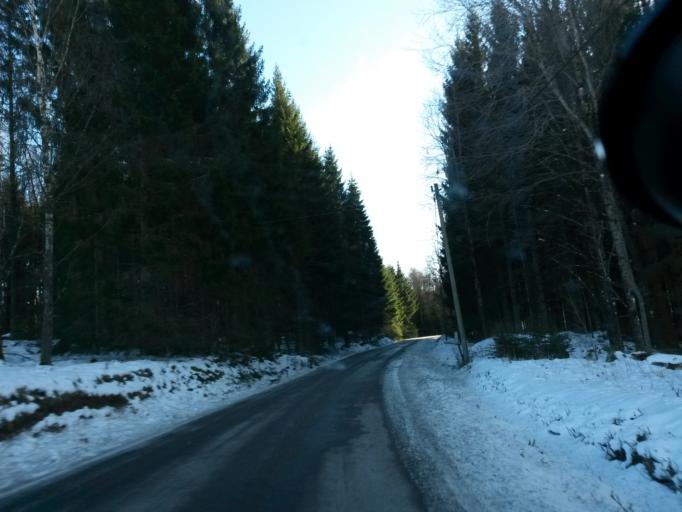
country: SE
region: Vaestra Goetaland
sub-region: Vargarda Kommun
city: Vargarda
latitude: 58.0277
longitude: 12.8937
